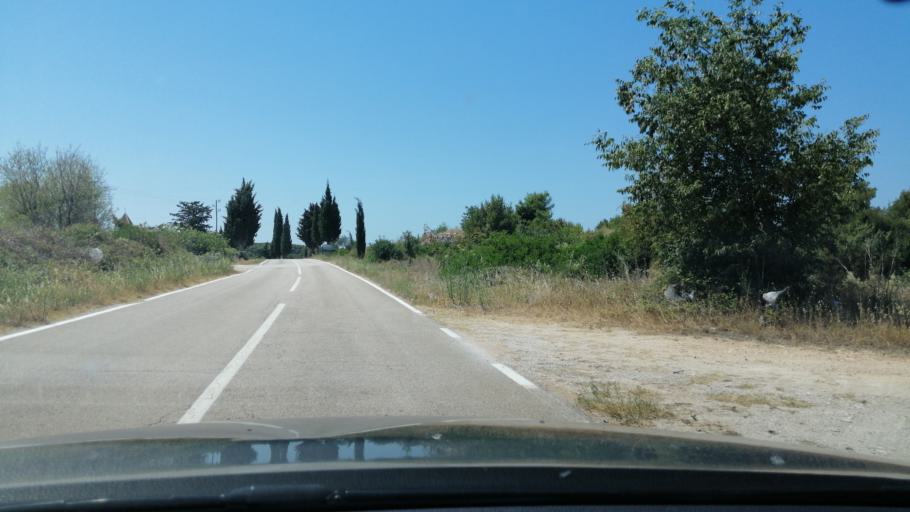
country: HR
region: Sibensko-Kniniska
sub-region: Grad Sibenik
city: Pirovac
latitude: 43.8302
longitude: 15.6812
